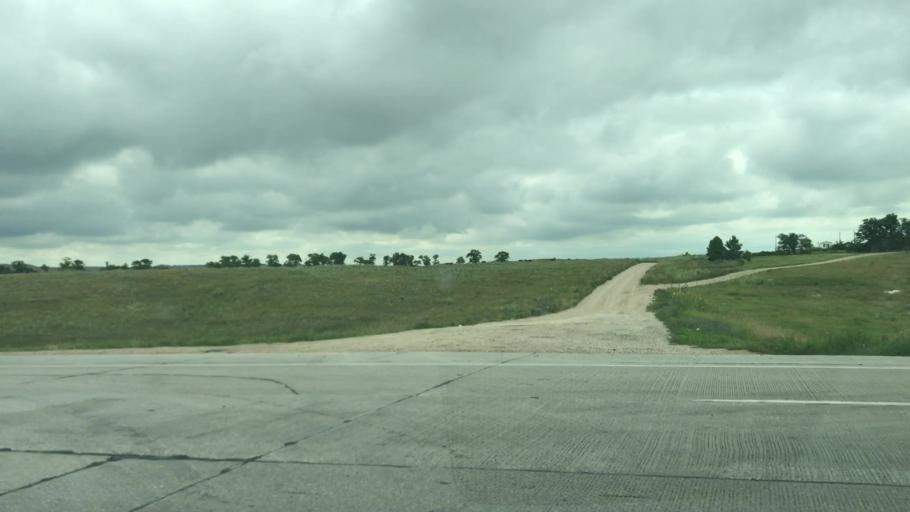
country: US
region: South Dakota
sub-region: Todd County
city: Mission
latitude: 43.3029
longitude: -100.7110
